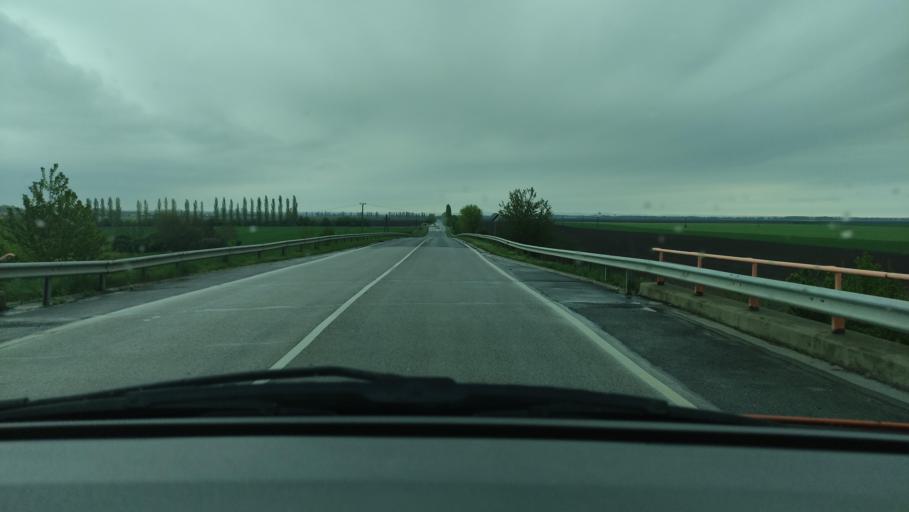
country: HU
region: Baranya
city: Mohacs
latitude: 45.9899
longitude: 18.6564
